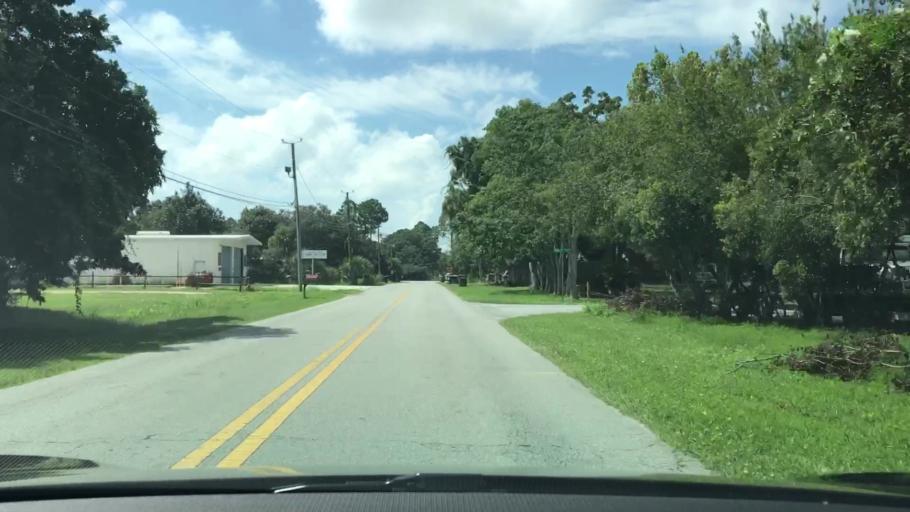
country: US
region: Florida
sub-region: Bay County
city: Panama City Beach
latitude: 30.1725
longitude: -85.7865
